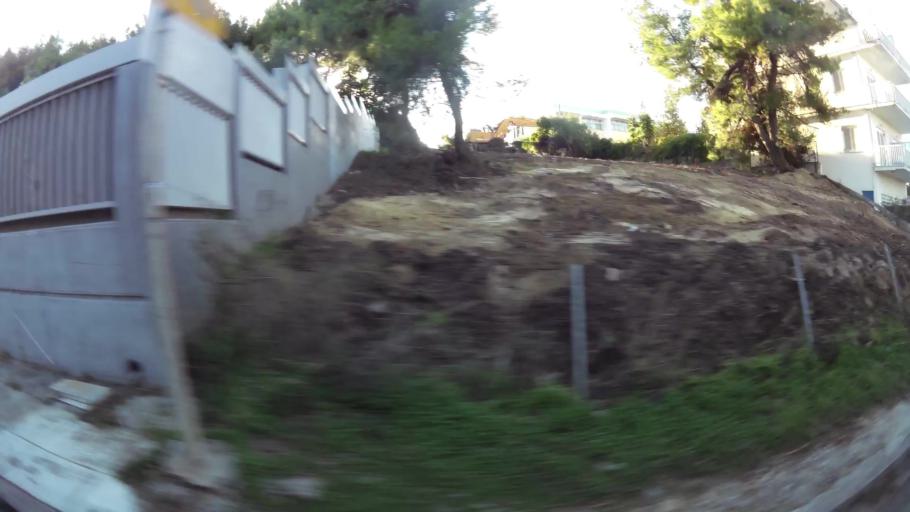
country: GR
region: Attica
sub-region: Nomarchia Anatolikis Attikis
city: Rafina
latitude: 38.0150
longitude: 24.0121
